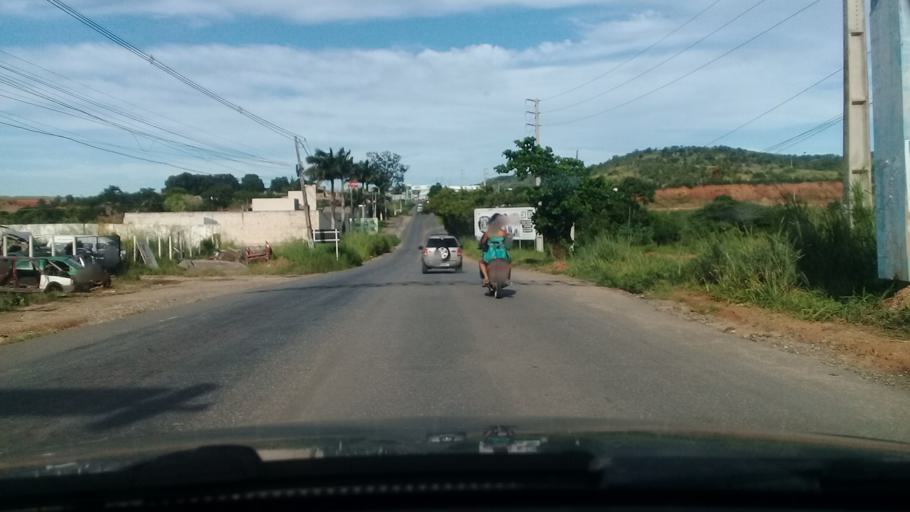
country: BR
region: Pernambuco
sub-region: Vitoria De Santo Antao
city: Vitoria de Santo Antao
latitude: -8.1159
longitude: -35.2693
